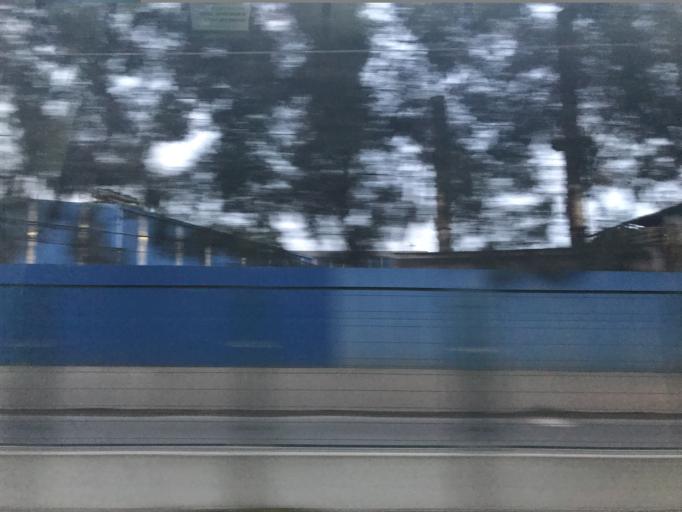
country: TR
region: Kocaeli
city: Darica
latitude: 40.8037
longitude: 29.3732
